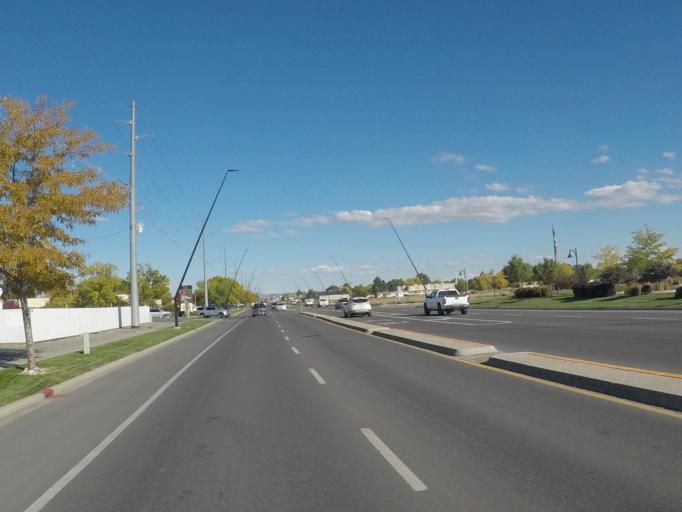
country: US
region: Montana
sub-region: Yellowstone County
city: Billings
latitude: 45.7842
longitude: -108.5968
